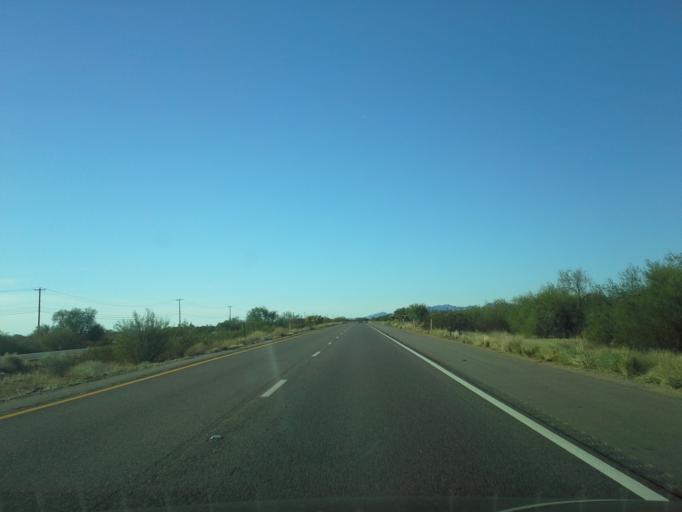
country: US
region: Arizona
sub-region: Pinal County
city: Gold Camp
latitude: 33.3075
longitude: -111.4063
